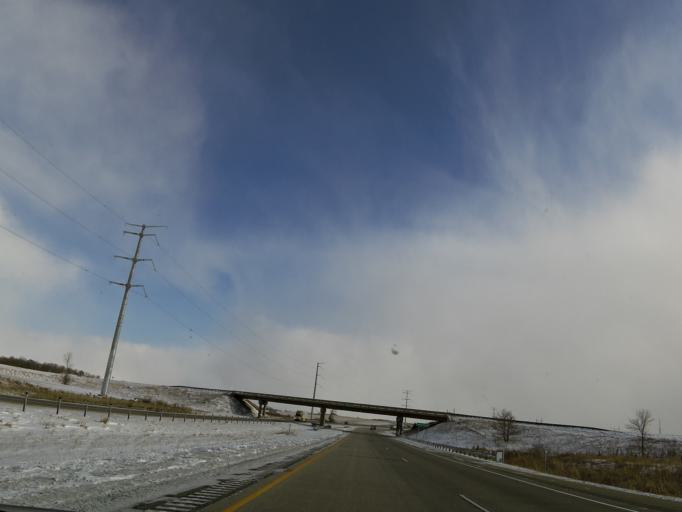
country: US
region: Minnesota
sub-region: Grant County
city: Elbow Lake
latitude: 46.1094
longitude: -95.8978
